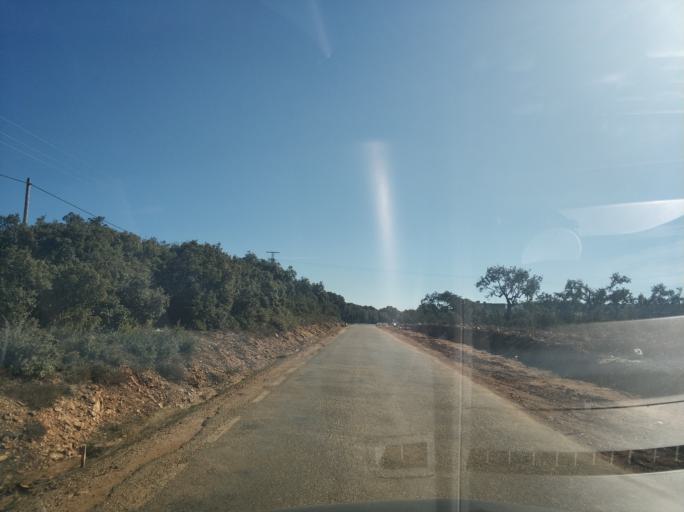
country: ES
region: Castille and Leon
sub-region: Provincia de Salamanca
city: Doninos de Salamanca
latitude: 40.9293
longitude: -5.7407
